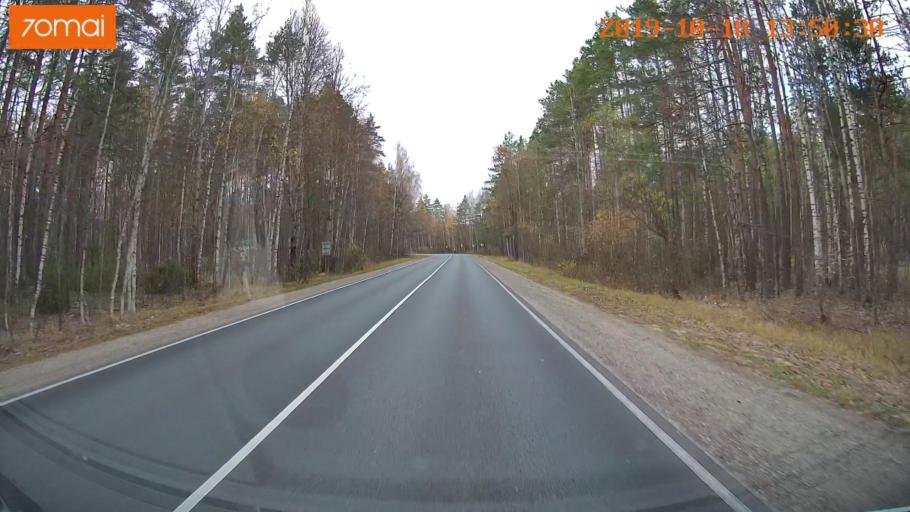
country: RU
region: Moskovskaya
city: Radovitskiy
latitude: 55.0068
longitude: 39.9705
